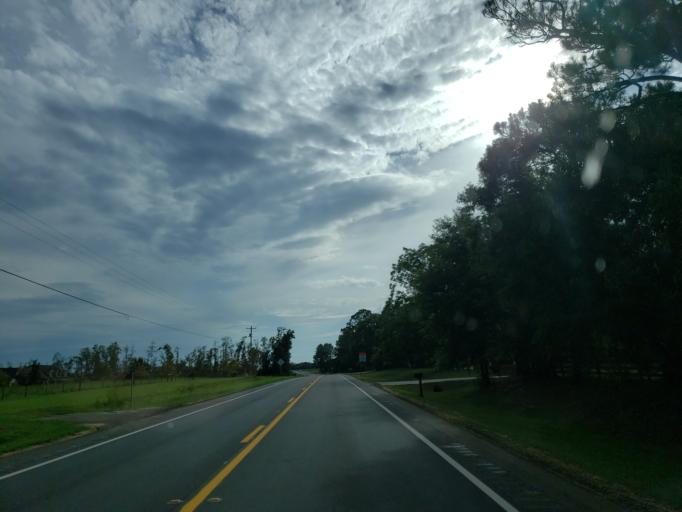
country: US
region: Georgia
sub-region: Irwin County
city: Ocilla
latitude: 31.5601
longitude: -83.3604
